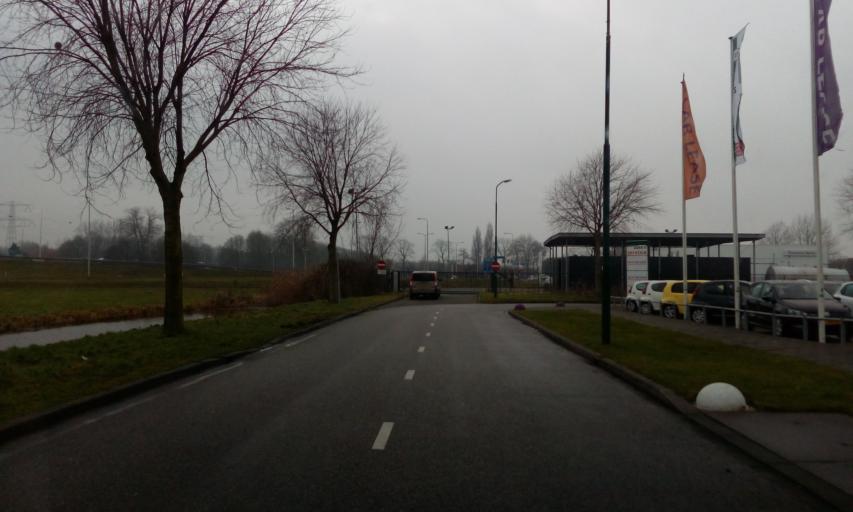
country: NL
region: Utrecht
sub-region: Gemeente Woerden
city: Woerden
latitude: 52.0735
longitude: 4.9050
